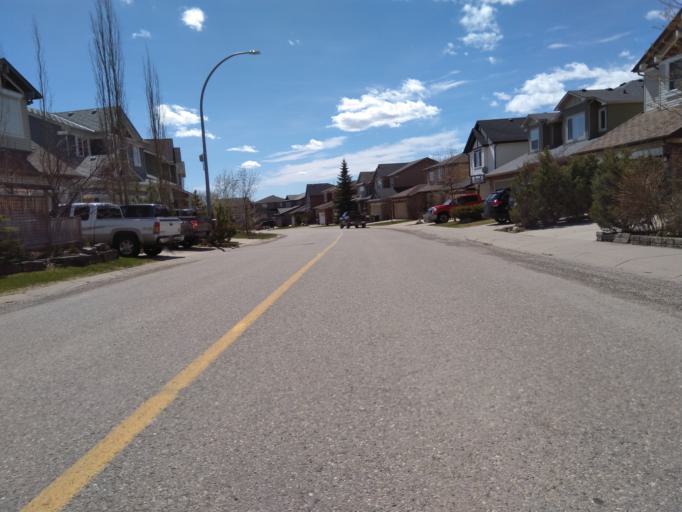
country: CA
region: Alberta
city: Calgary
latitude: 51.1343
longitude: -114.2495
